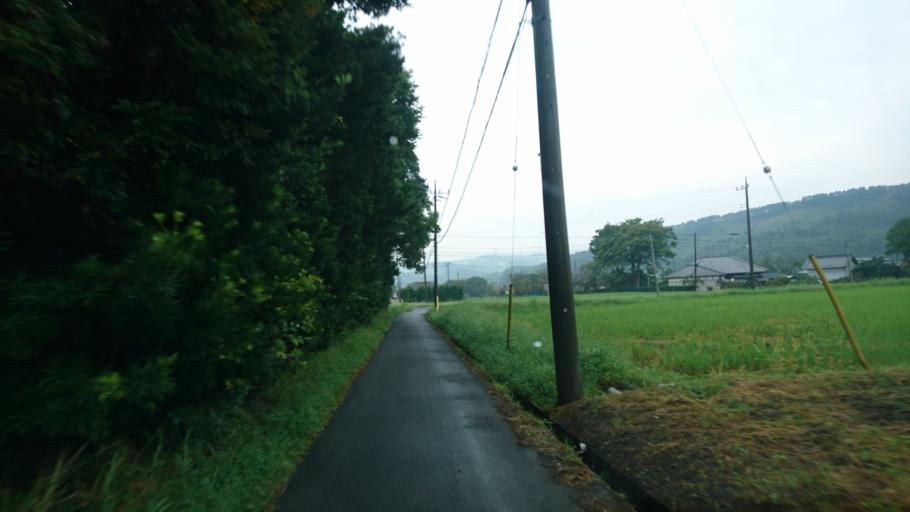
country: JP
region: Chiba
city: Kimitsu
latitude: 35.2916
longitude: 139.9866
